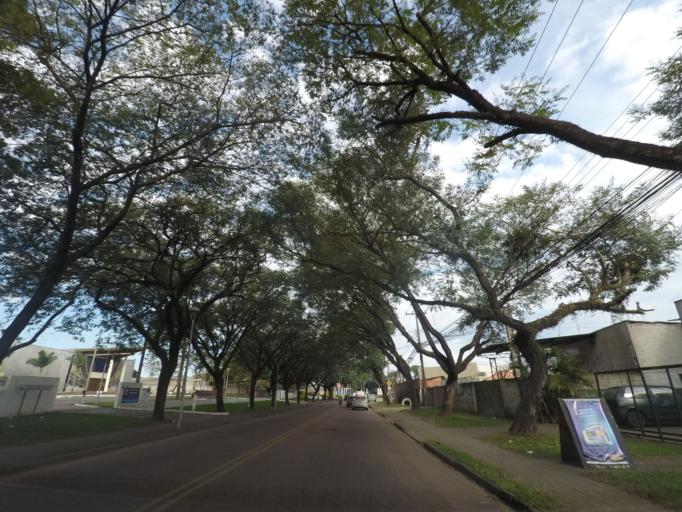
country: BR
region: Parana
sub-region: Sao Jose Dos Pinhais
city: Sao Jose dos Pinhais
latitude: -25.5333
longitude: -49.2966
